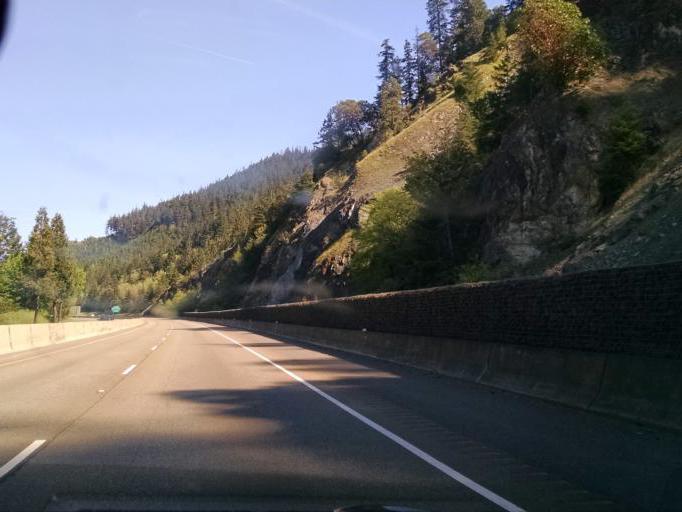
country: US
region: Oregon
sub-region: Douglas County
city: Myrtle Creek
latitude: 43.0308
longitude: -123.3192
